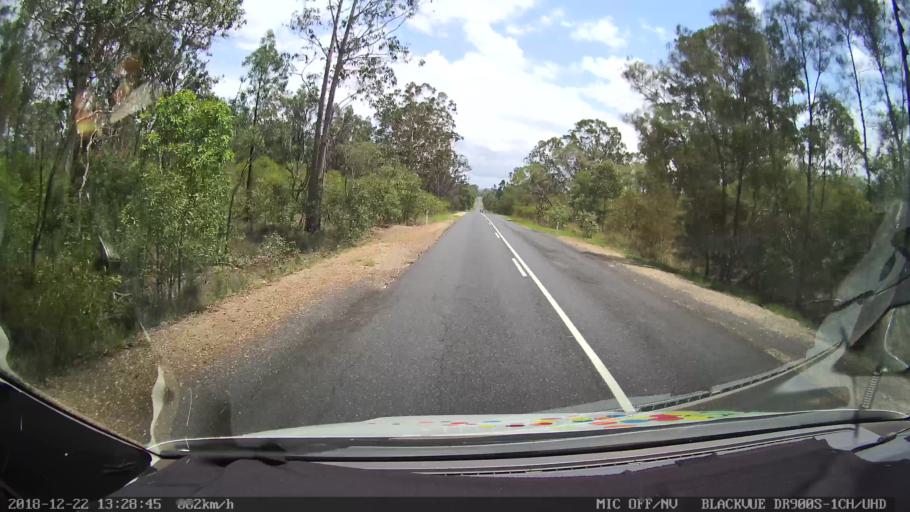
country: AU
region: New South Wales
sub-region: Clarence Valley
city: Coutts Crossing
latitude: -29.8366
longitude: 152.8850
